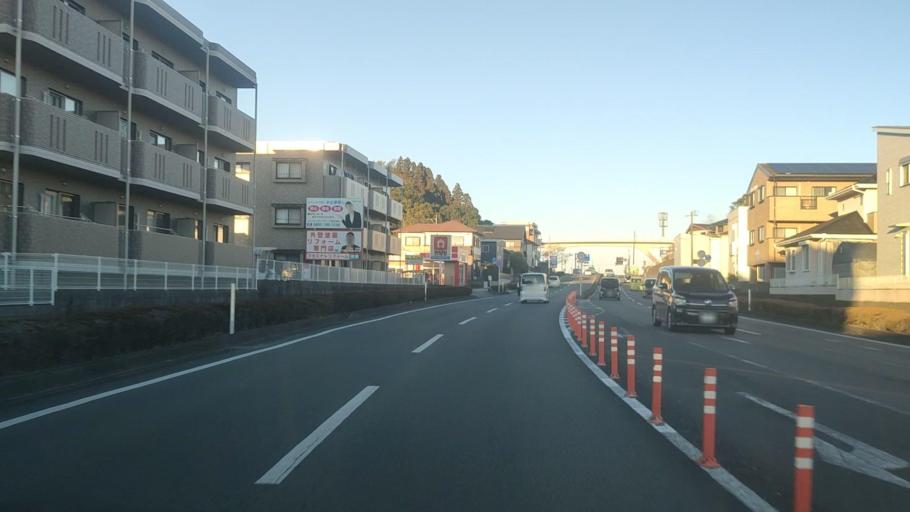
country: JP
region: Miyazaki
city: Miyazaki-shi
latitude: 31.9031
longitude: 131.4066
